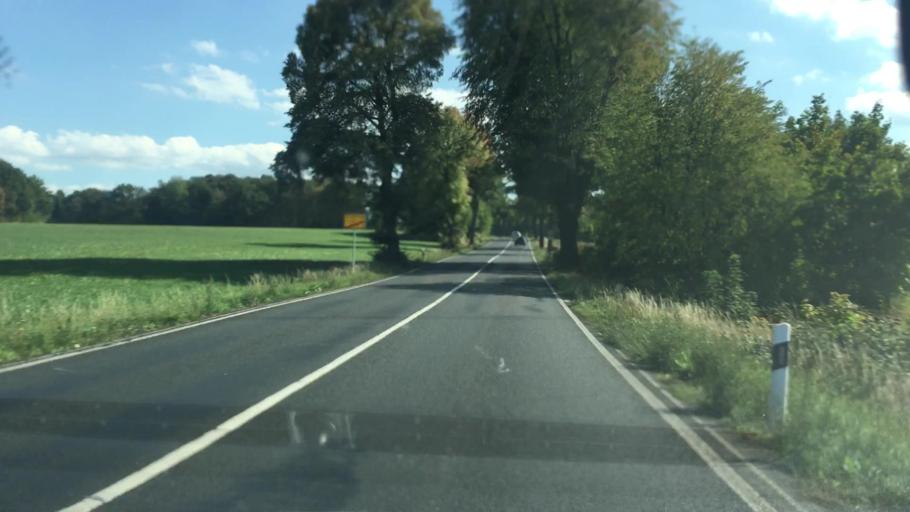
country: DE
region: Saxony
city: Dohma
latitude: 50.8959
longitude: 13.9459
